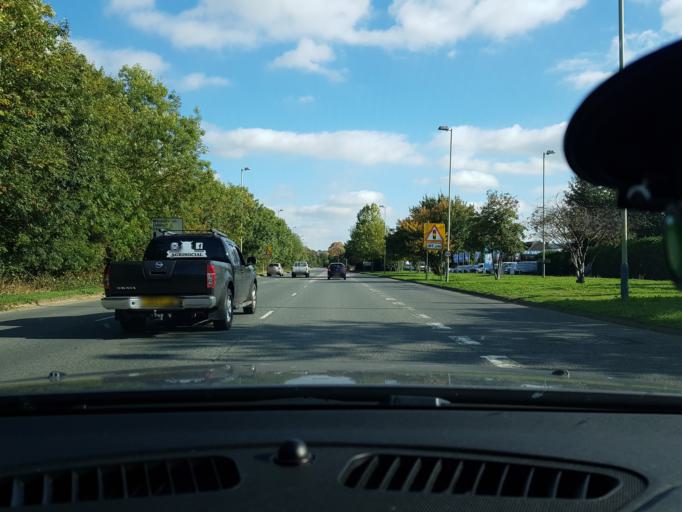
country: GB
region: England
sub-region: Borough of Swindon
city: Chiseldon
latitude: 51.5429
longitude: -1.7311
